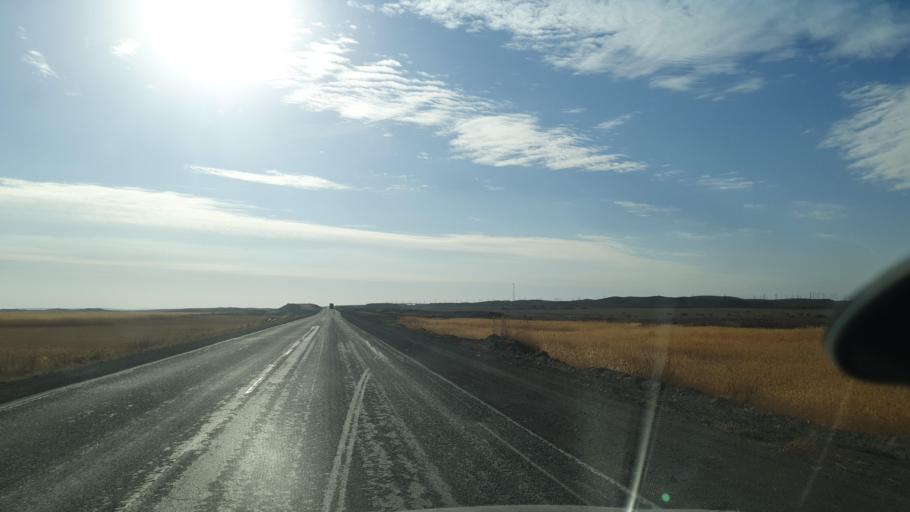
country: KZ
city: Priozersk
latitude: 45.8336
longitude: 73.4535
